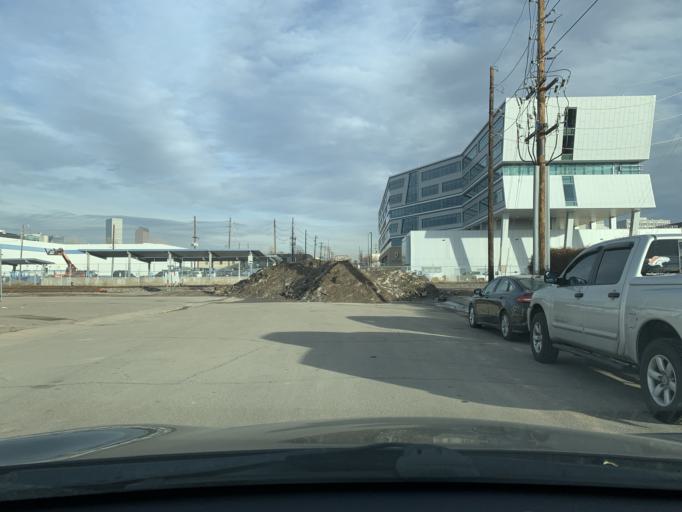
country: US
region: Colorado
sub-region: Denver County
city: Denver
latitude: 39.7352
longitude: -105.0116
